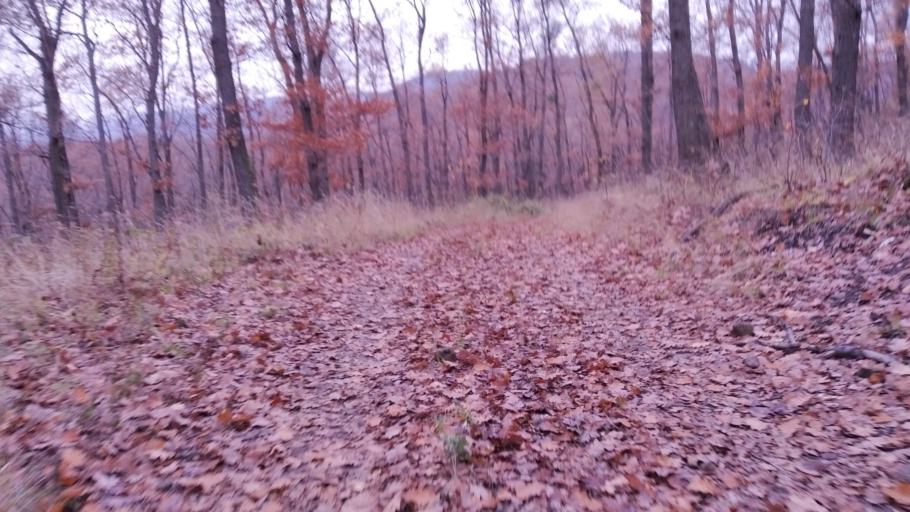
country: HU
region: Pest
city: Csobanka
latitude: 47.6777
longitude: 18.9560
